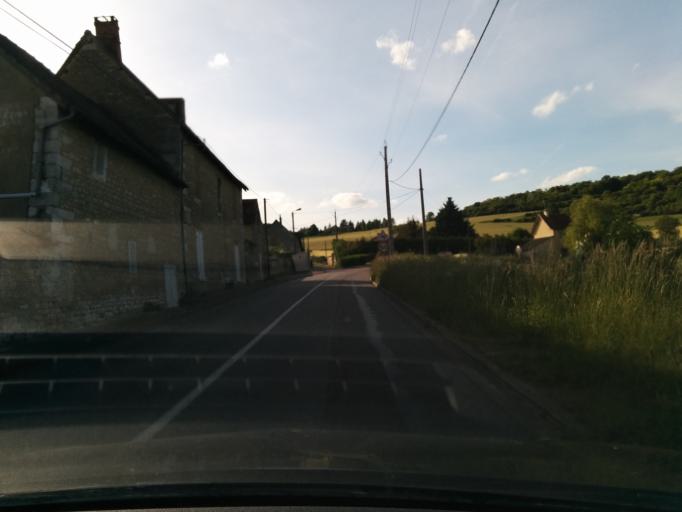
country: FR
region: Haute-Normandie
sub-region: Departement de l'Eure
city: Courcelles-sur-Seine
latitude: 49.1734
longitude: 1.3966
